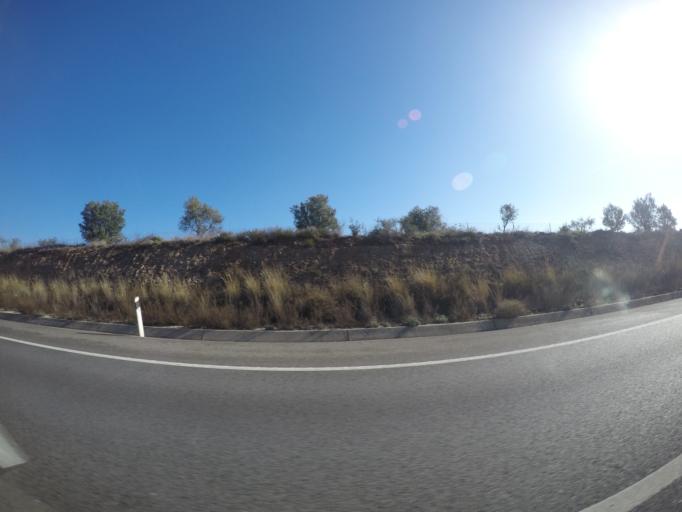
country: ES
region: Catalonia
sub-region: Provincia de Barcelona
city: Esparreguera
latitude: 41.5414
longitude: 1.8568
